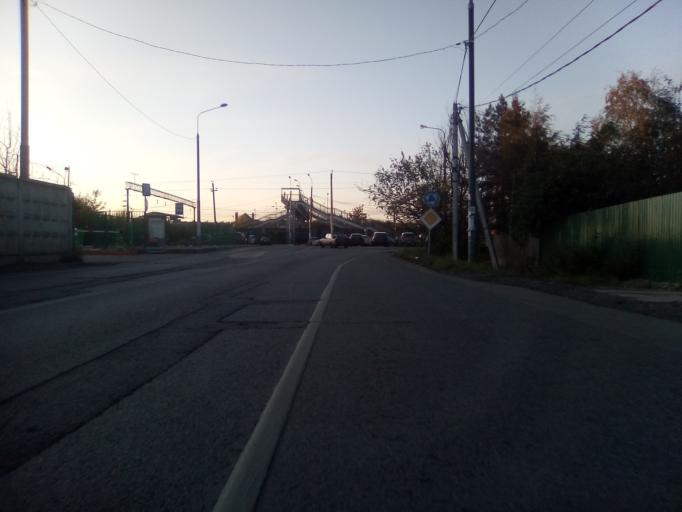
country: RU
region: Moskovskaya
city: Kokoshkino
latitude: 55.6067
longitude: 37.1871
